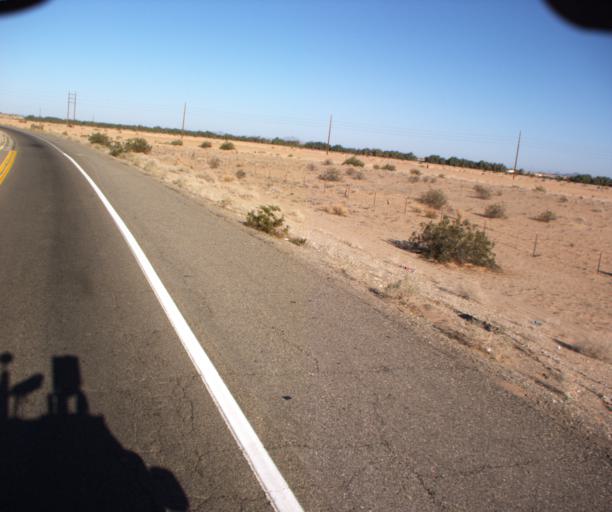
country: US
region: Arizona
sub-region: Yuma County
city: Fortuna Foothills
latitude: 32.6741
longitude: -114.4862
